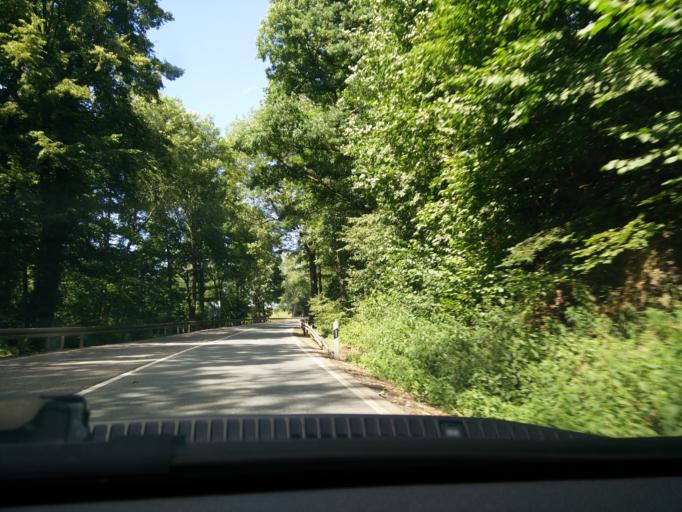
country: DE
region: Saxony
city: Penig
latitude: 50.9343
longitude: 12.6846
